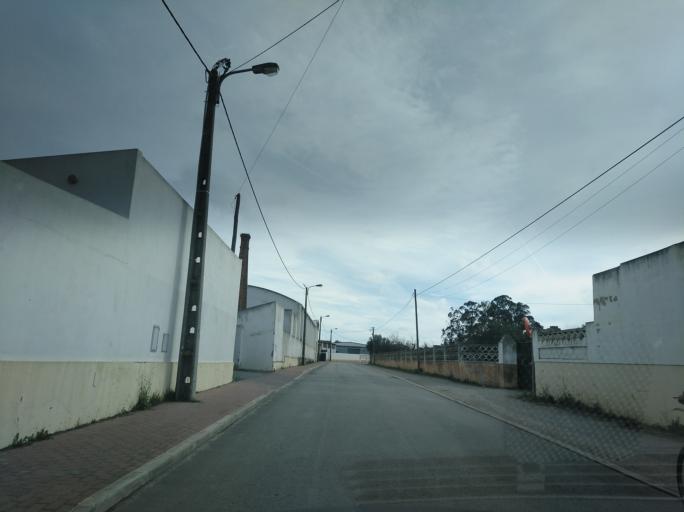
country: PT
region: Setubal
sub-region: Grandola
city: Grandola
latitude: 38.1834
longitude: -8.5558
